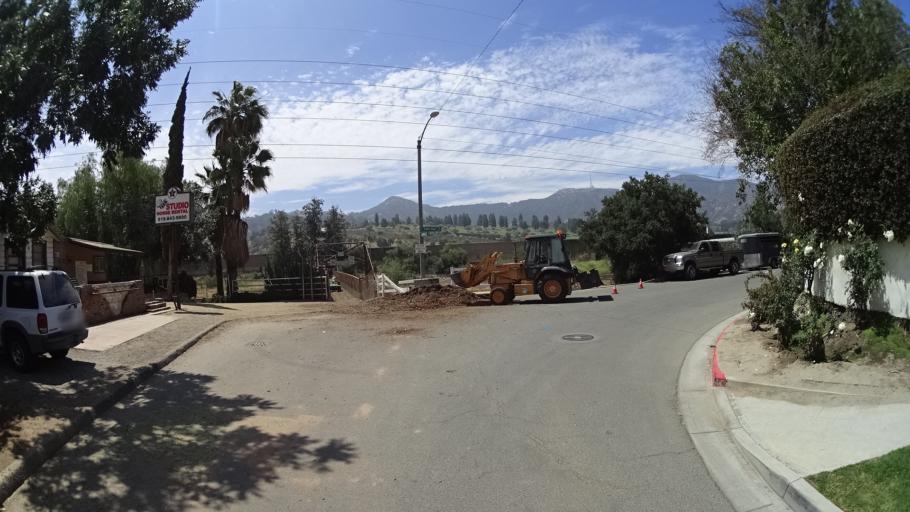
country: US
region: California
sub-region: Los Angeles County
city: Burbank
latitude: 34.1559
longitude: -118.3129
